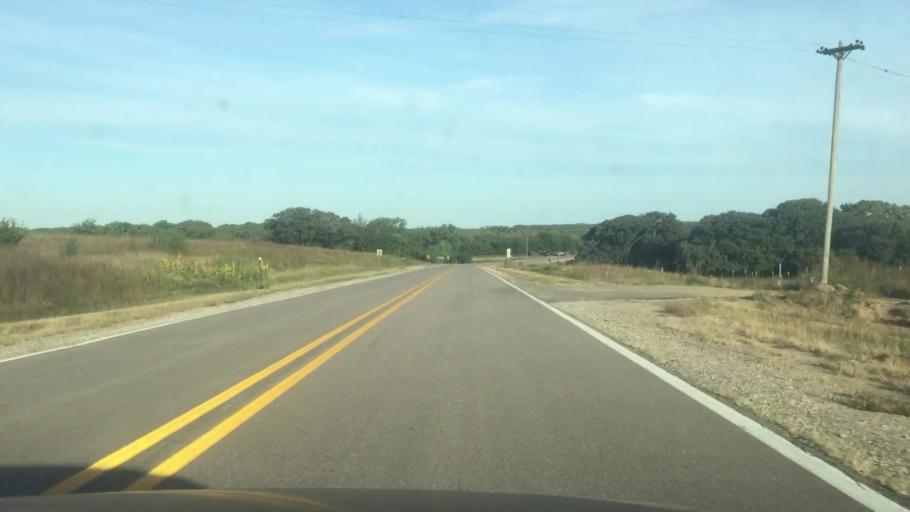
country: US
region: Nebraska
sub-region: Jefferson County
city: Fairbury
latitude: 40.0430
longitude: -97.0202
